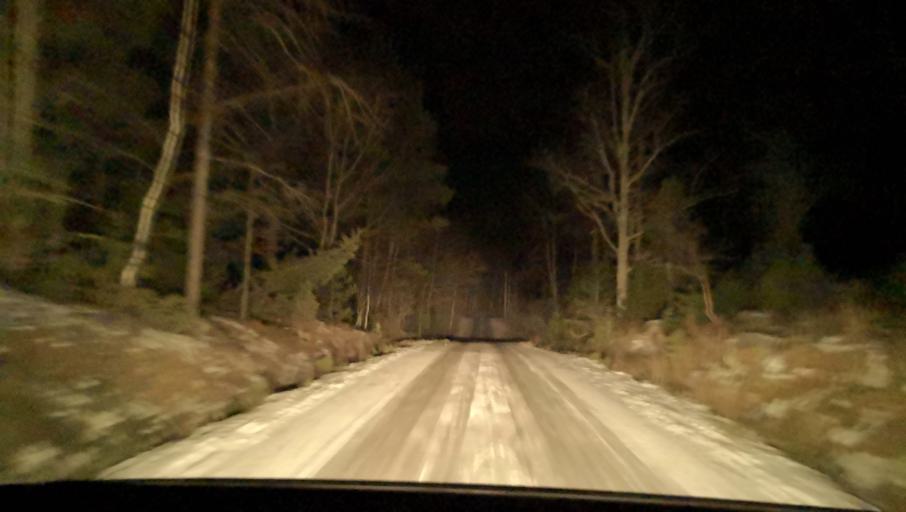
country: SE
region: Stockholm
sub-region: Tyreso Kommun
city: Bollmora
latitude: 59.2778
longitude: 18.2284
